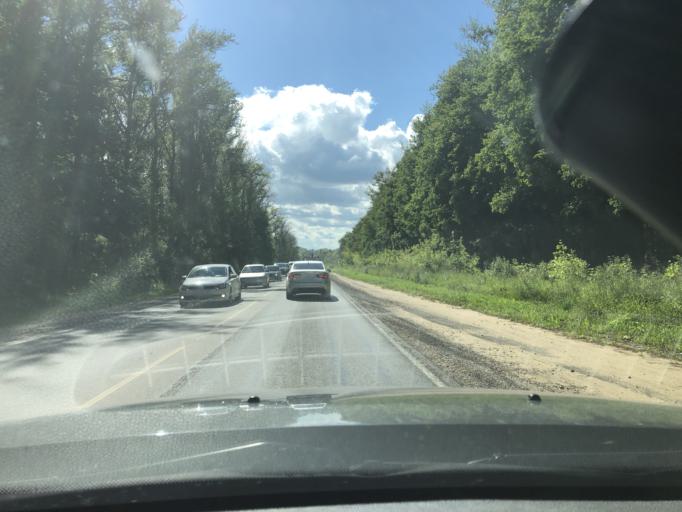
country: RU
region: Tula
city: Donskoy
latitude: 53.9696
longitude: 38.3948
